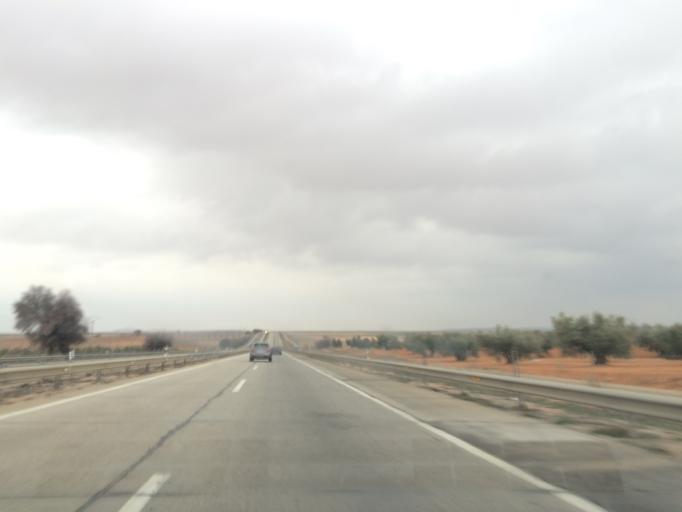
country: ES
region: Castille-La Mancha
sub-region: Province of Toledo
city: Madridejos
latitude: 39.5364
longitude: -3.5200
